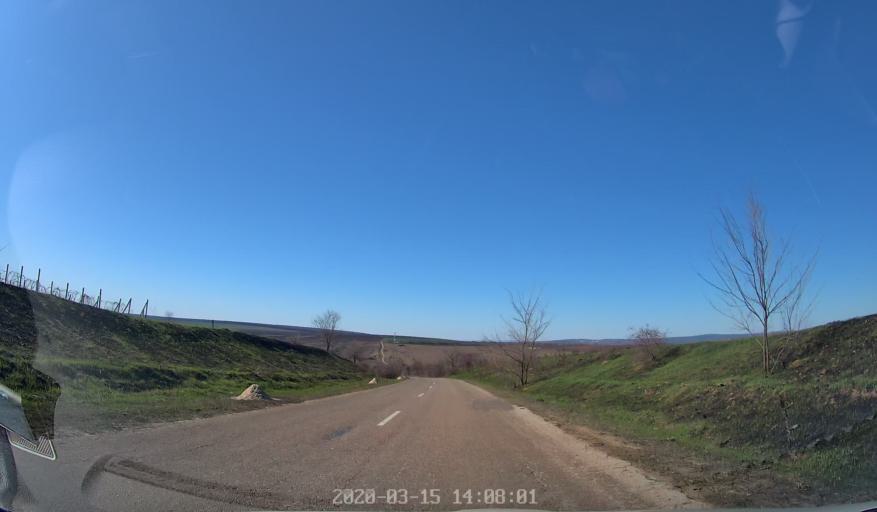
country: MD
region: Orhei
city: Orhei
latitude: 47.3060
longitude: 28.9425
